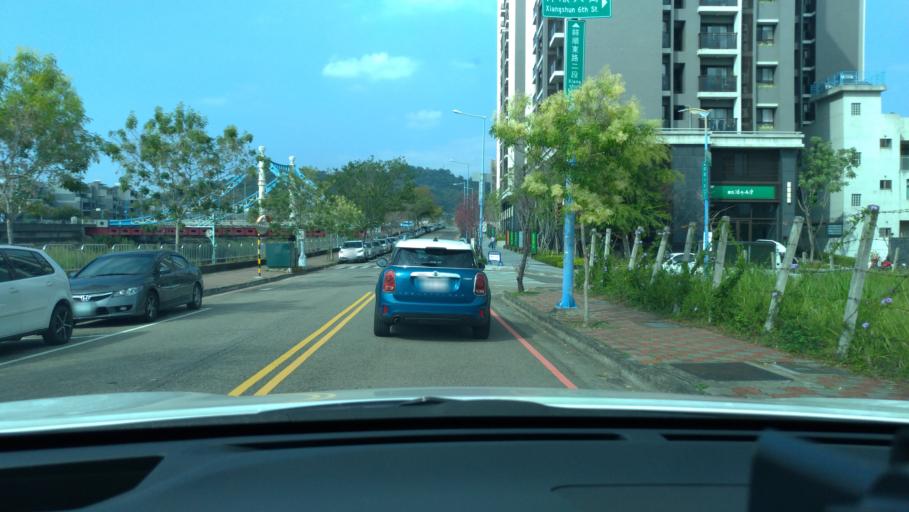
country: TW
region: Taiwan
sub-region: Taichung City
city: Taichung
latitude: 24.1695
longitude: 120.7289
